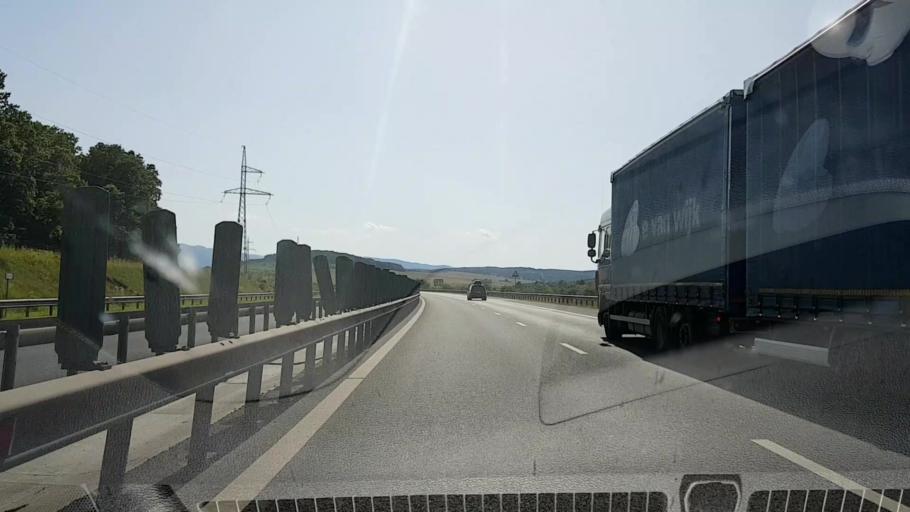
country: RO
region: Sibiu
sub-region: Comuna Cristian
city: Cristian
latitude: 45.8033
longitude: 24.0406
